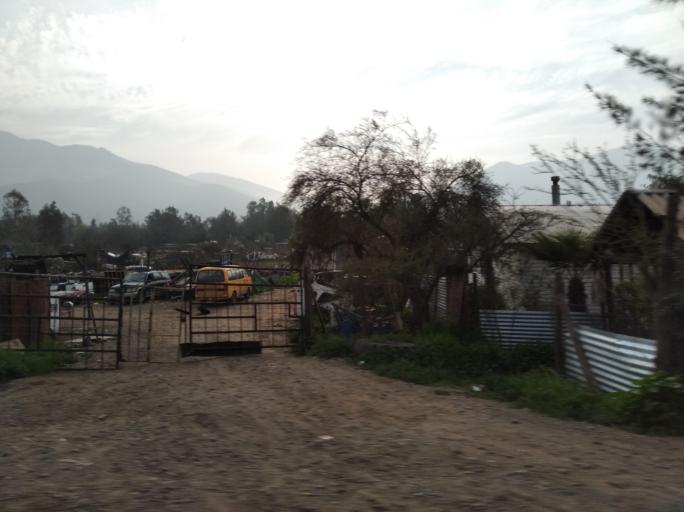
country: CL
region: Santiago Metropolitan
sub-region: Provincia de Chacabuco
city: Lampa
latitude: -33.2690
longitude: -70.8943
